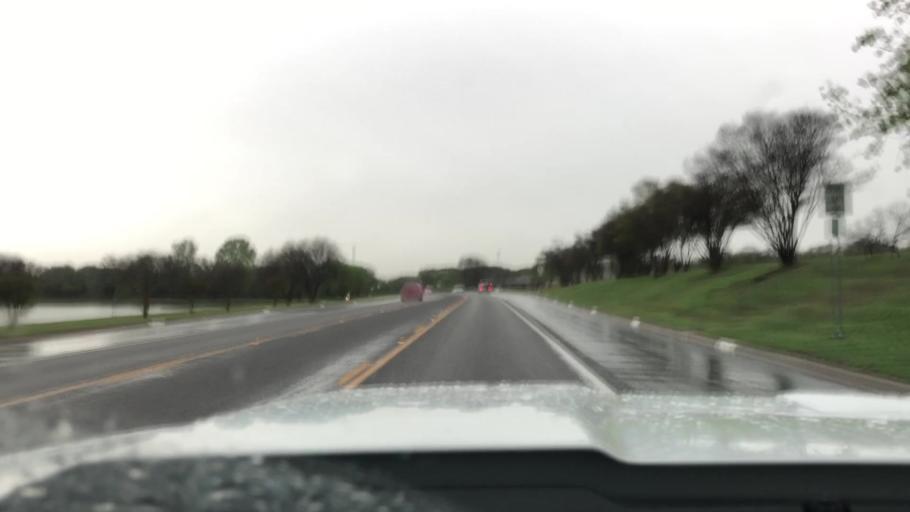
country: US
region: Texas
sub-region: Johnson County
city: Keene
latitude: 32.4003
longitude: -97.3288
